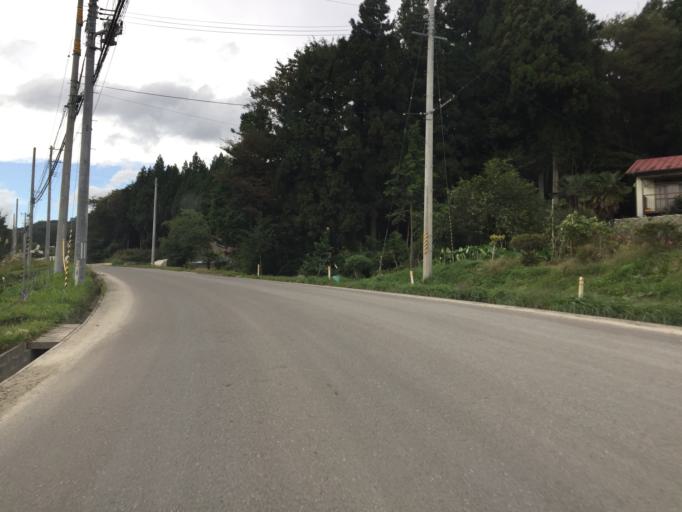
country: JP
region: Miyagi
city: Marumori
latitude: 37.9000
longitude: 140.7218
